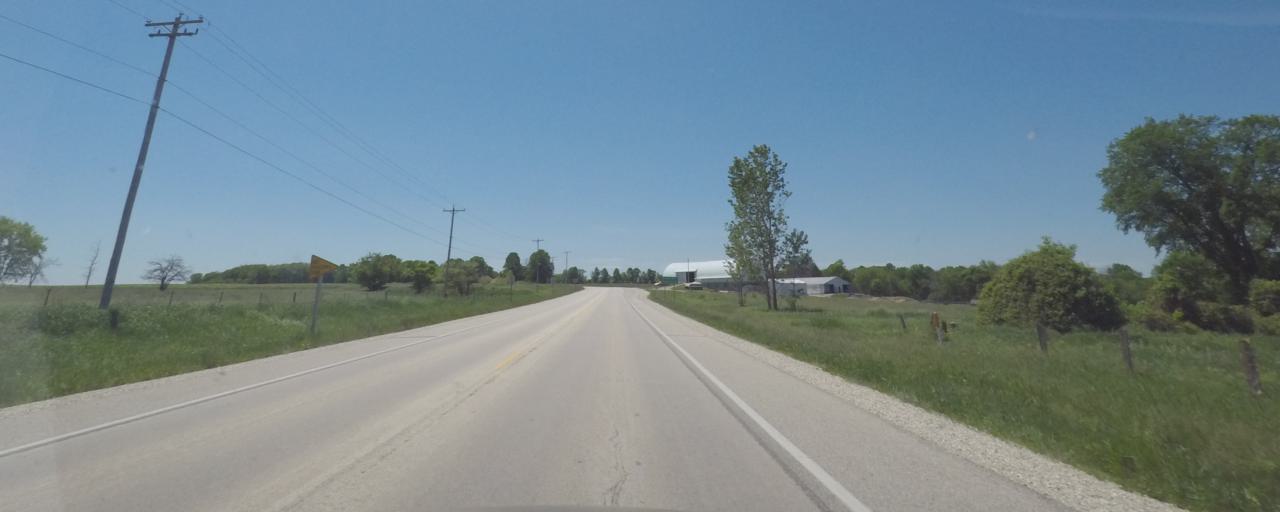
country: US
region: Wisconsin
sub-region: Ozaukee County
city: Kohler
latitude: 43.5146
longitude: -88.1138
